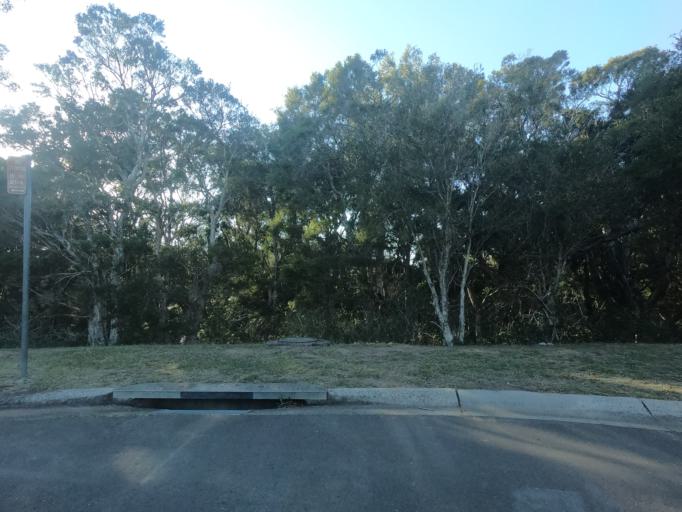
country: AU
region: New South Wales
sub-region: Wollongong
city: Dapto
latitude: -34.4948
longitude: 150.7789
